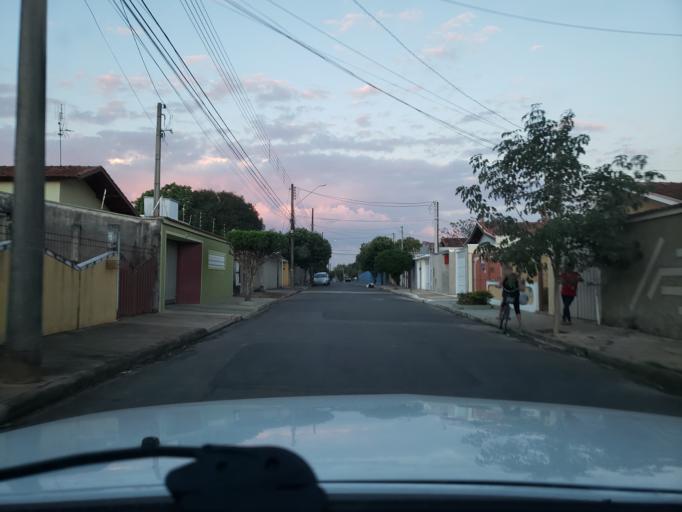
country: BR
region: Sao Paulo
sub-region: Moji-Guacu
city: Mogi-Gaucu
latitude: -22.3427
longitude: -46.9440
